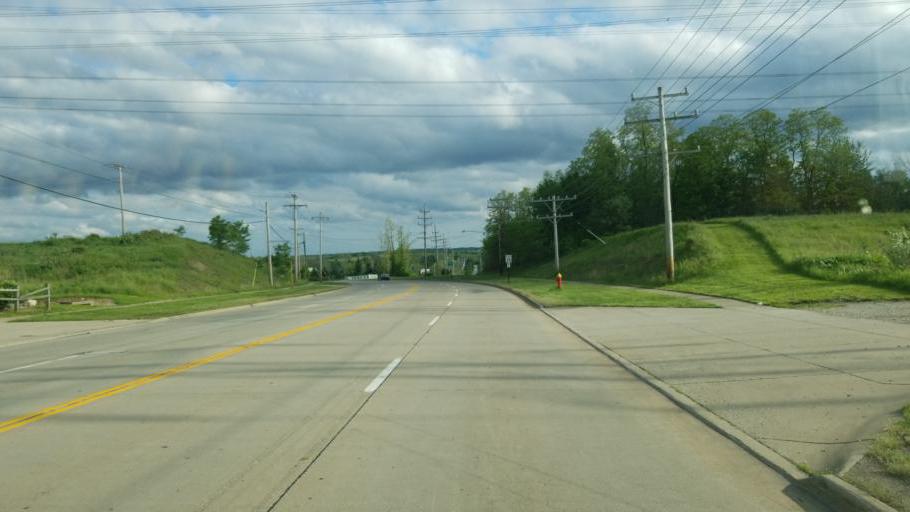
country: US
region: Ohio
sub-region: Cuyahoga County
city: Solon
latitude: 41.3660
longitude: -81.4697
